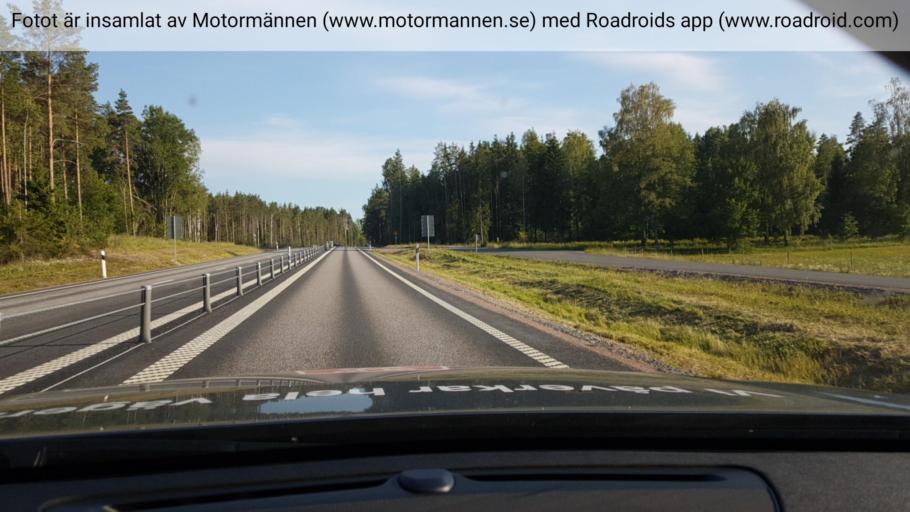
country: SE
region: Uppsala
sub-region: Osthammars Kommun
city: Gimo
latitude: 60.1019
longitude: 18.1252
